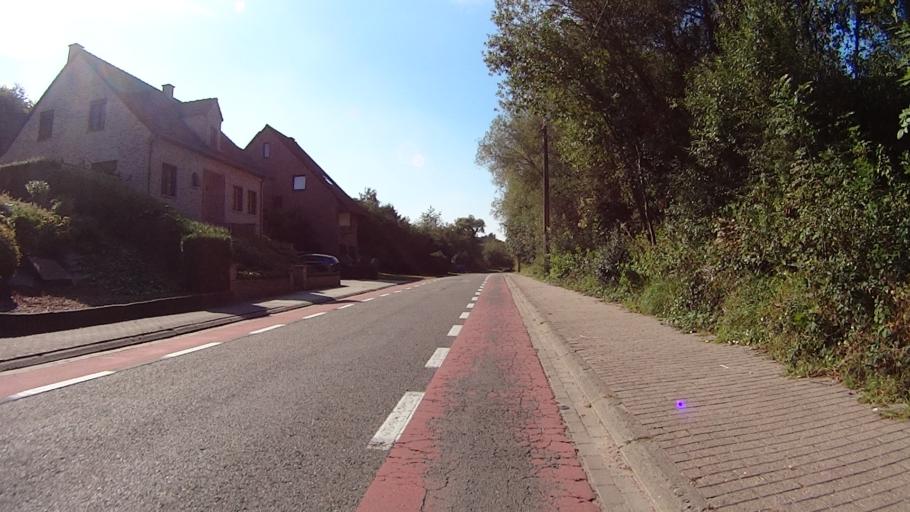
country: BE
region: Flanders
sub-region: Provincie Vlaams-Brabant
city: Hoeilaart
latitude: 50.7672
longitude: 4.4907
